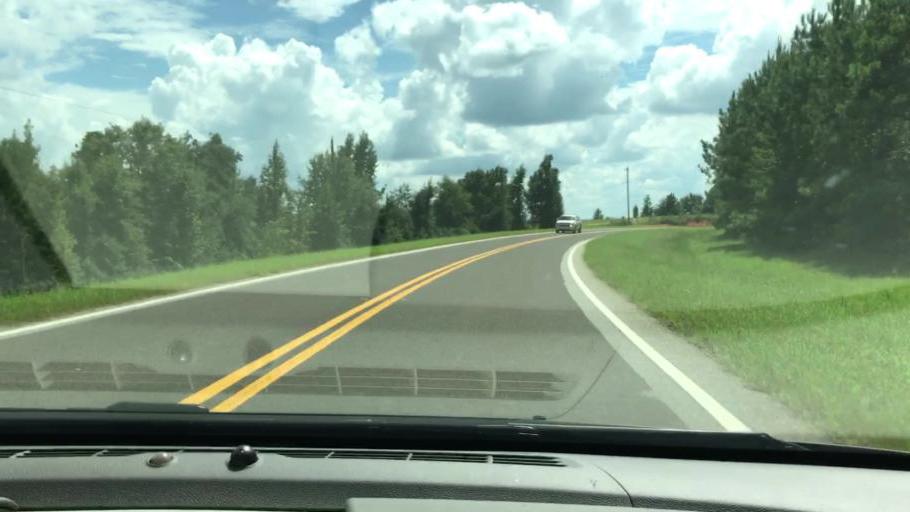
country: US
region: Georgia
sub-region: Quitman County
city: Georgetown
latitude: 31.9121
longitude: -85.0594
